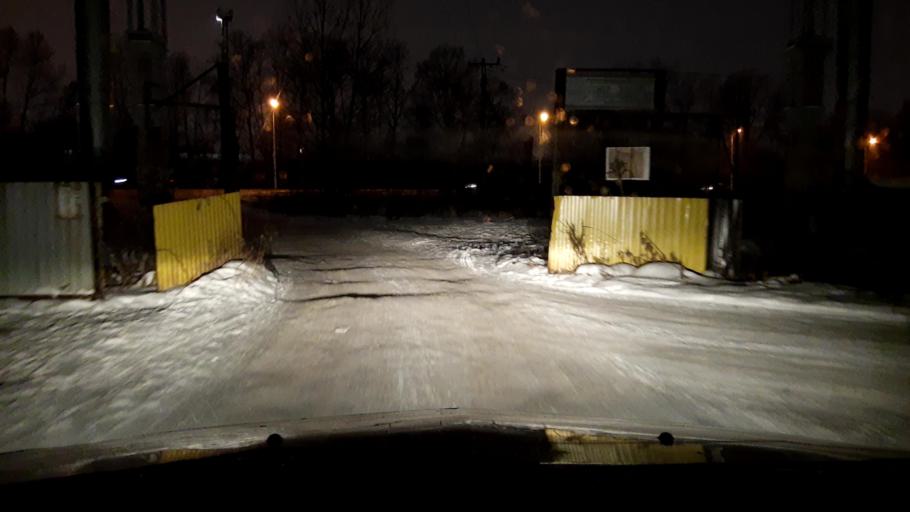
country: RU
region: Bashkortostan
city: Ufa
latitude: 54.8372
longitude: 56.1338
